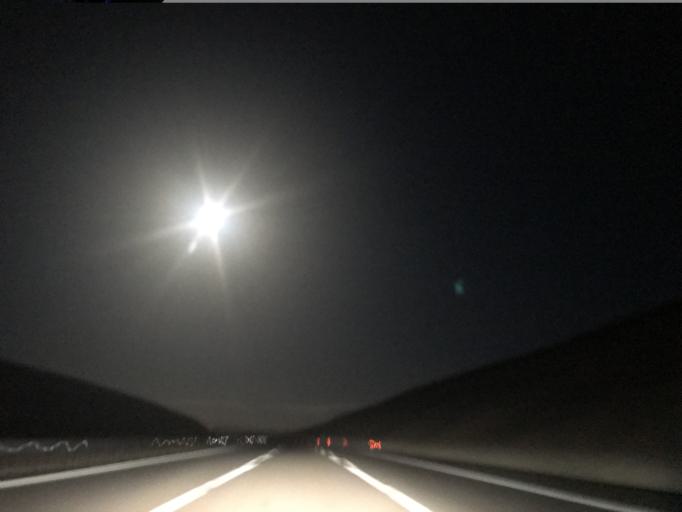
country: TR
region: Nigde
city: Ulukisla
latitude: 37.6354
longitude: 34.4111
